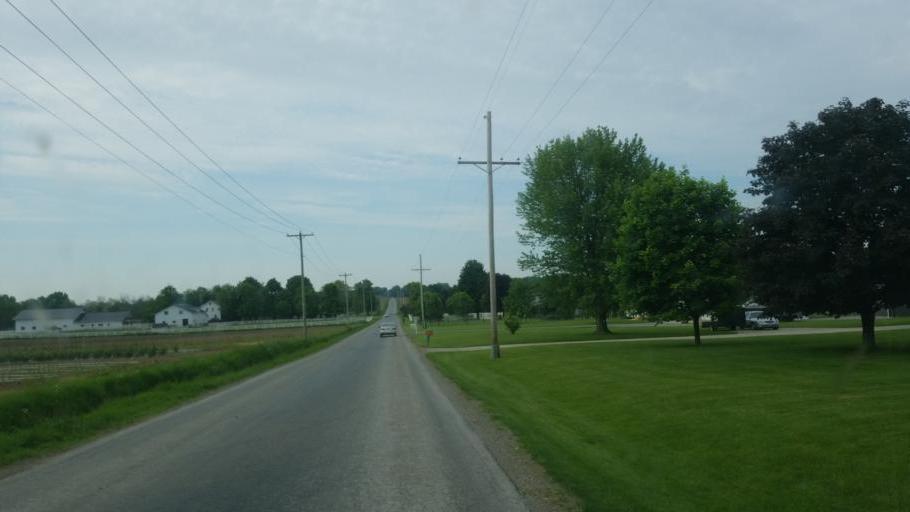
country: US
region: Ohio
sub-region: Wayne County
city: Dalton
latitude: 40.7520
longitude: -81.7548
